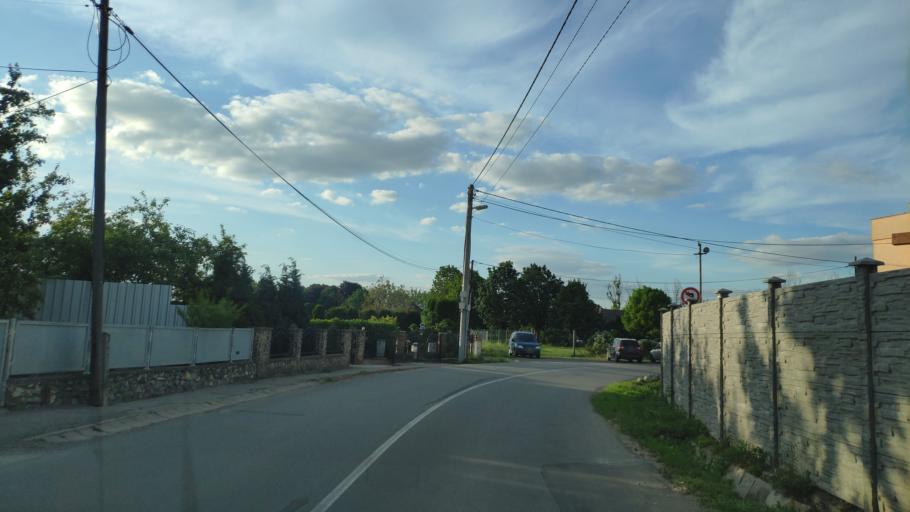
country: SK
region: Kosicky
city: Kosice
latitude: 48.6494
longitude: 21.3196
